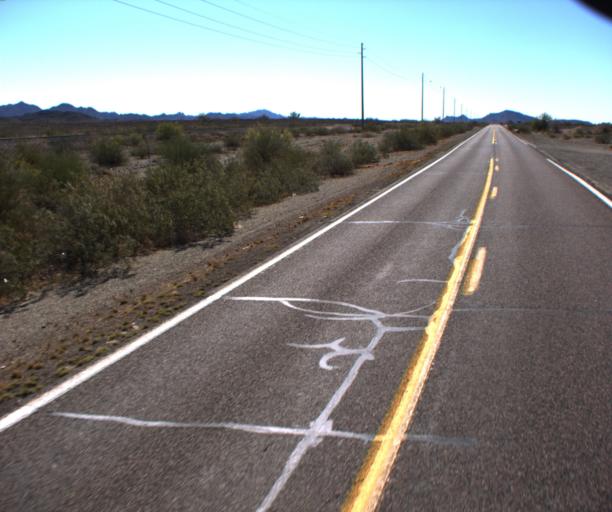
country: US
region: Arizona
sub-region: La Paz County
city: Salome
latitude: 33.7689
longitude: -113.7914
